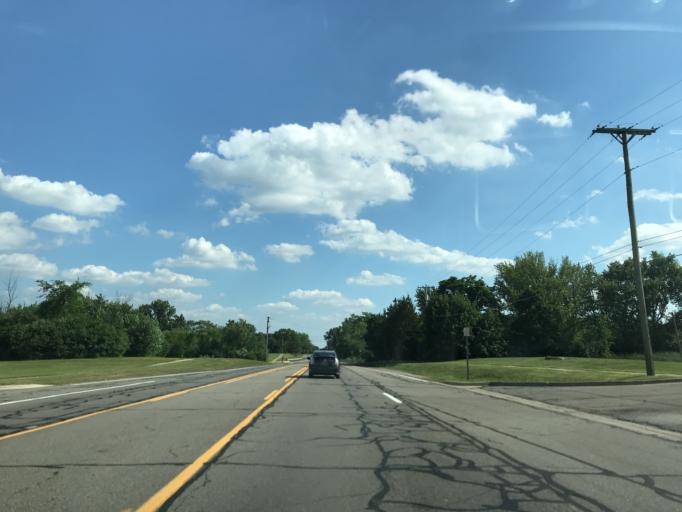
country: US
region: Michigan
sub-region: Oakland County
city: Farmington Hills
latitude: 42.4789
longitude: -83.3381
